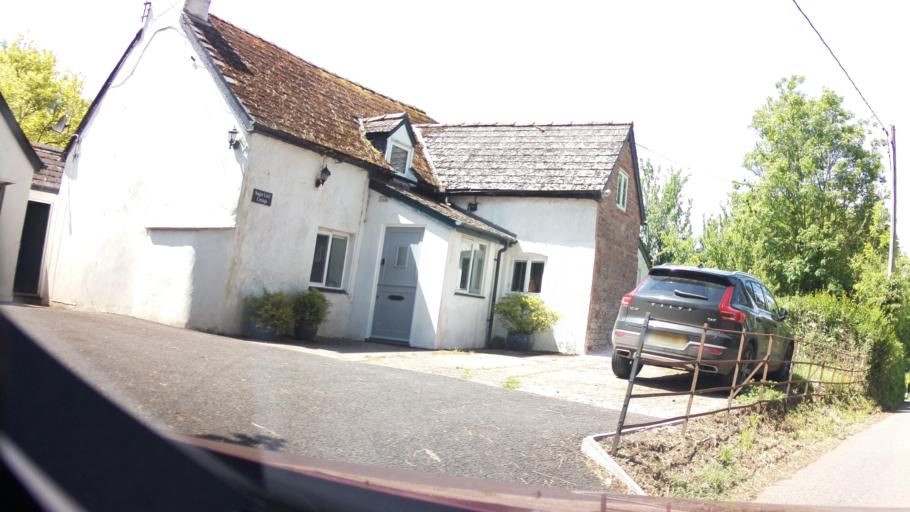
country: GB
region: Wales
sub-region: Monmouthshire
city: Monmouth
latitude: 51.8283
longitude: -2.7503
